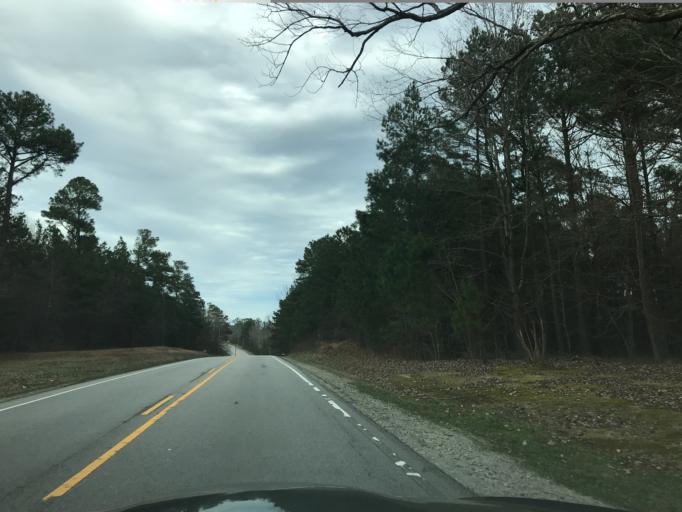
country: US
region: North Carolina
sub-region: Franklin County
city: Louisburg
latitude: 36.0759
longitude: -78.3233
